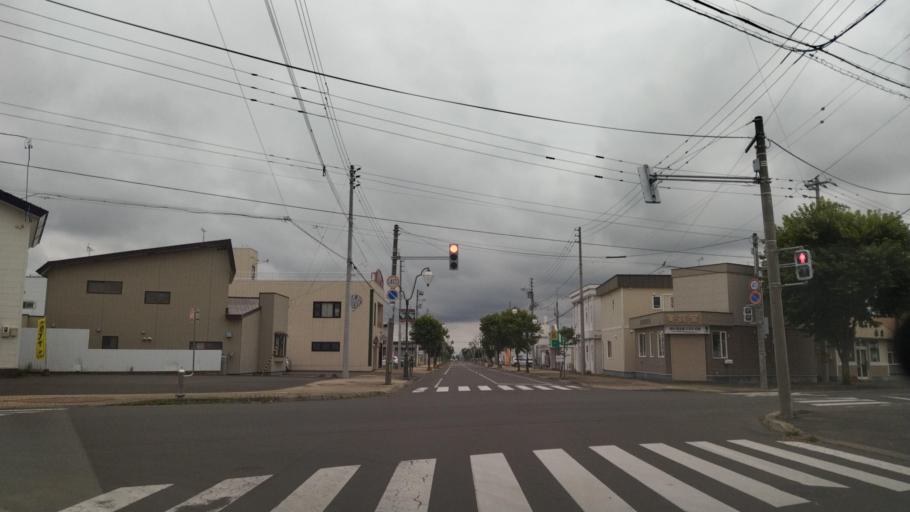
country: JP
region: Hokkaido
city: Otofuke
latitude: 43.2340
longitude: 143.2924
